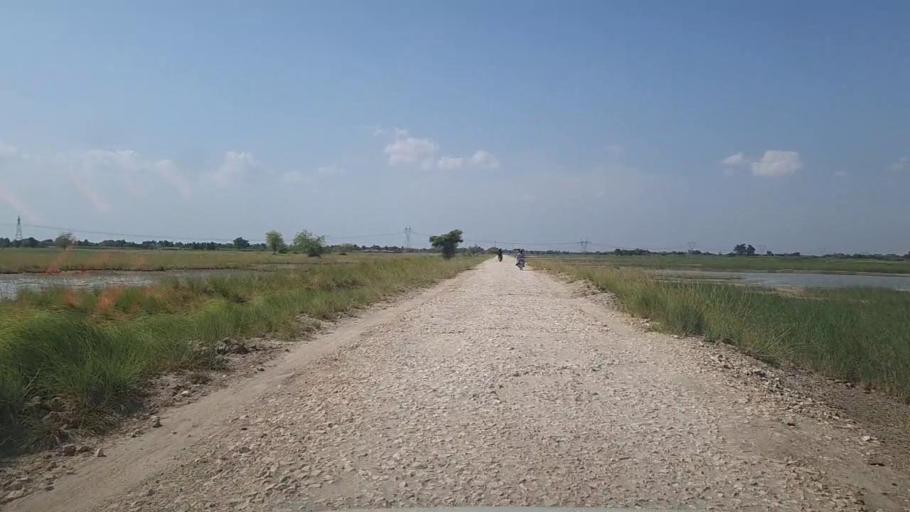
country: PK
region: Sindh
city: Khairpur
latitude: 28.1006
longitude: 69.6258
